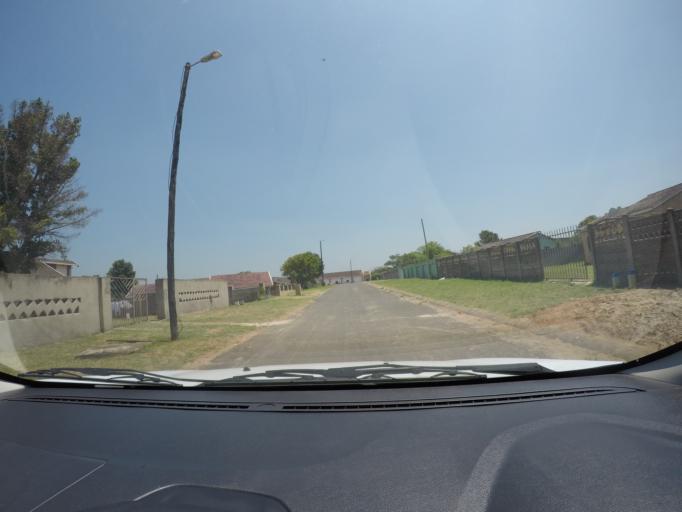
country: ZA
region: KwaZulu-Natal
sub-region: uThungulu District Municipality
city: eSikhawini
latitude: -28.8737
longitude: 31.9116
